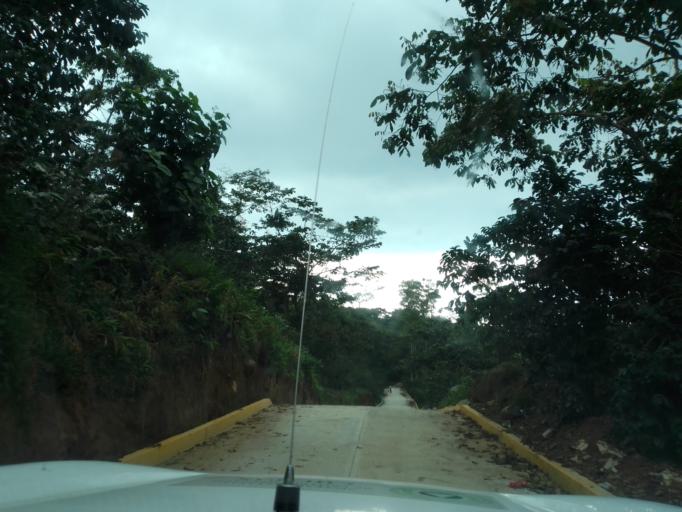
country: MX
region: Chiapas
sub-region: Union Juarez
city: Santo Domingo
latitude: 15.0658
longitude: -92.1165
